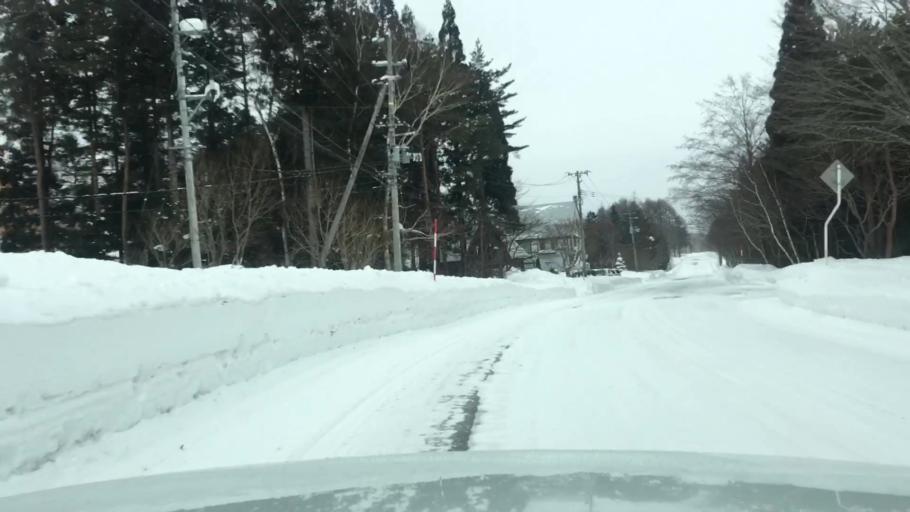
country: JP
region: Akita
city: Hanawa
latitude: 40.0033
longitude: 140.9816
